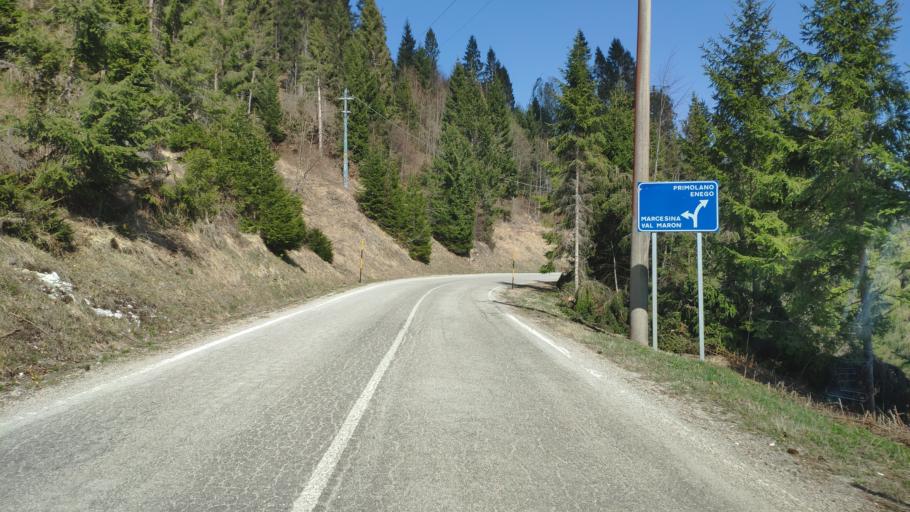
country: IT
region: Veneto
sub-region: Provincia di Vicenza
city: Enego
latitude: 45.9321
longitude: 11.6833
